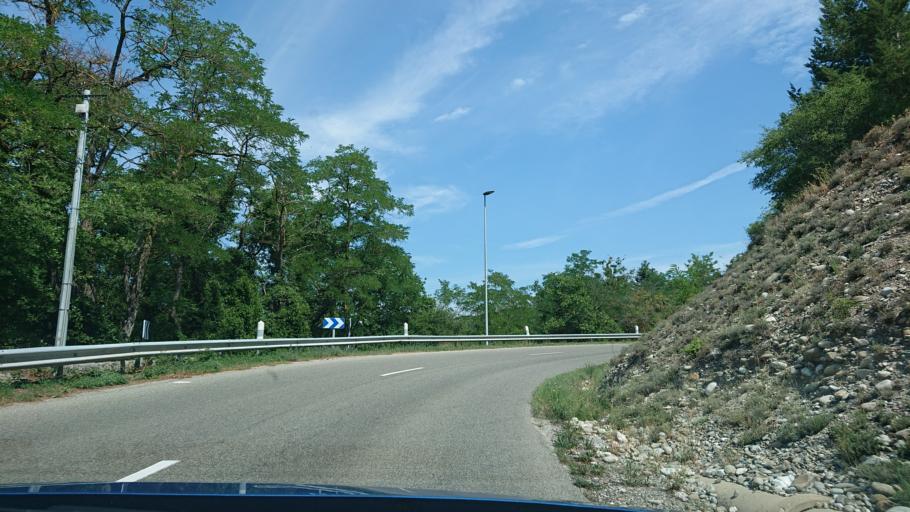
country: FR
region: Provence-Alpes-Cote d'Azur
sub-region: Departement des Alpes-de-Haute-Provence
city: Sisteron
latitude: 44.2212
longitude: 5.9375
